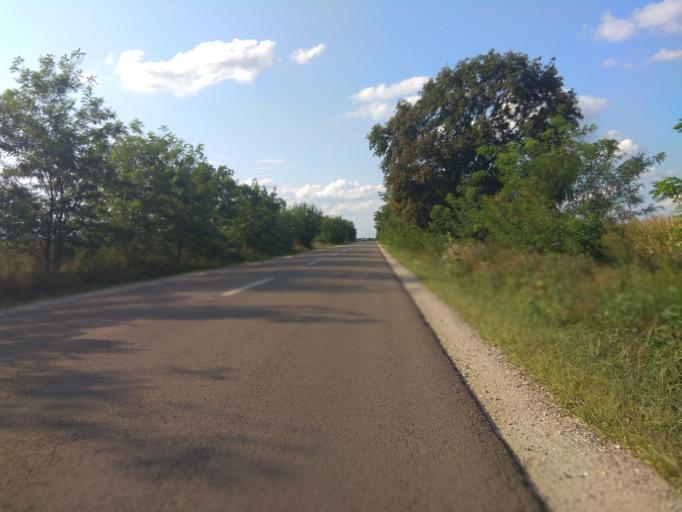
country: HU
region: Borsod-Abauj-Zemplen
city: Hejobaba
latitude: 47.9149
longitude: 20.8830
